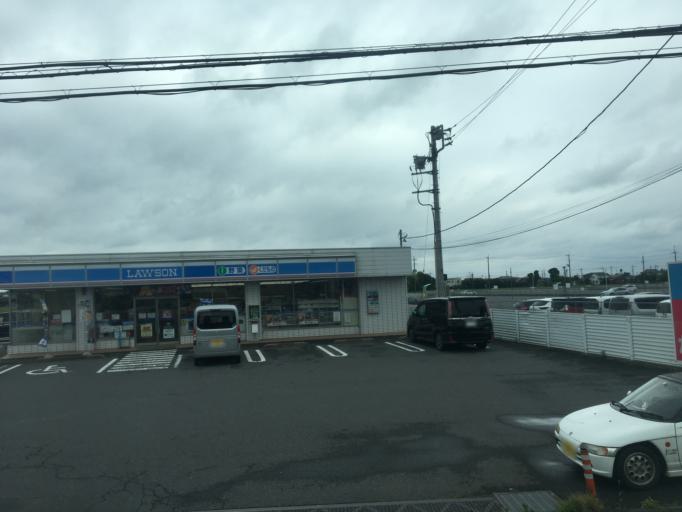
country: JP
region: Saitama
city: Kawagoe
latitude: 35.9338
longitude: 139.5217
